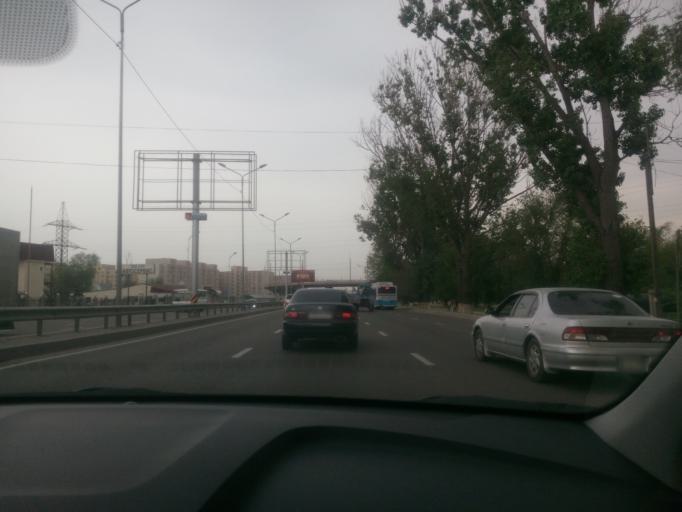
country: KZ
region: Almaty Qalasy
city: Almaty
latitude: 43.2391
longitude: 76.8119
